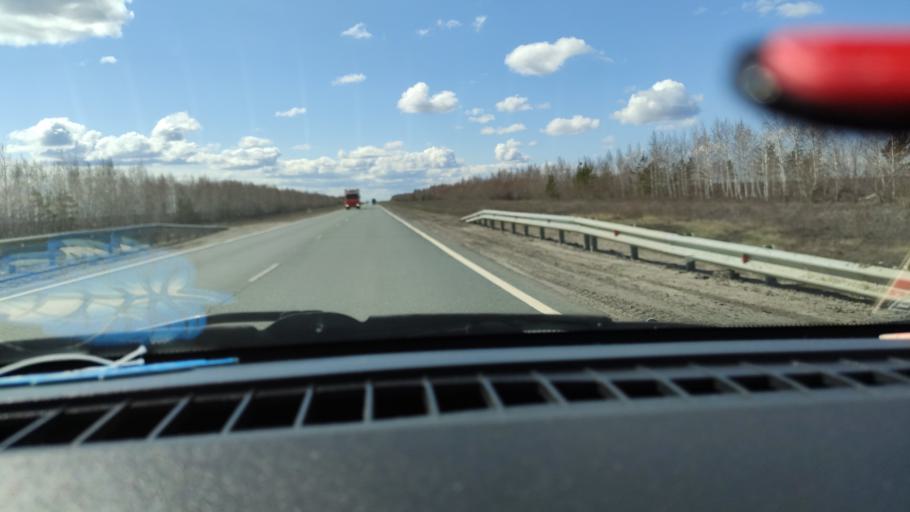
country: RU
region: Saratov
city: Dukhovnitskoye
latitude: 52.8195
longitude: 48.2335
